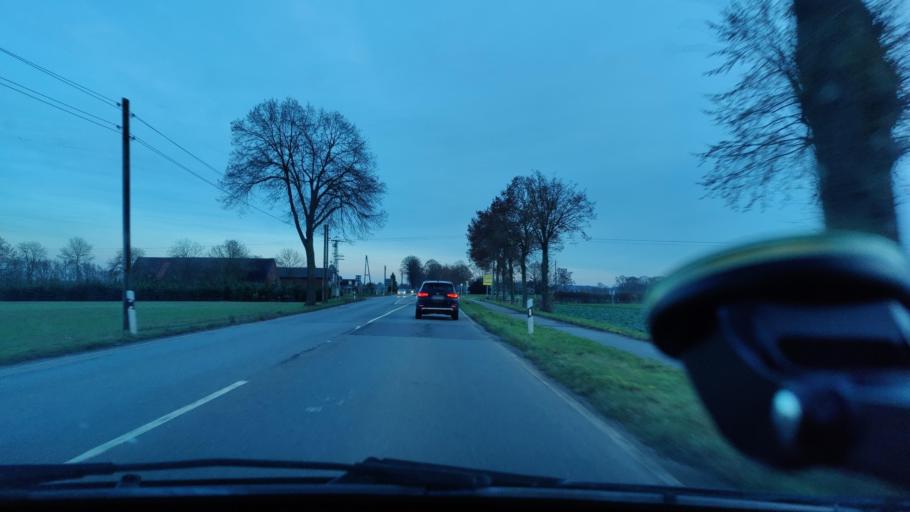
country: DE
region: North Rhine-Westphalia
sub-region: Regierungsbezirk Dusseldorf
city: Xanten
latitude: 51.6807
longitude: 6.4144
